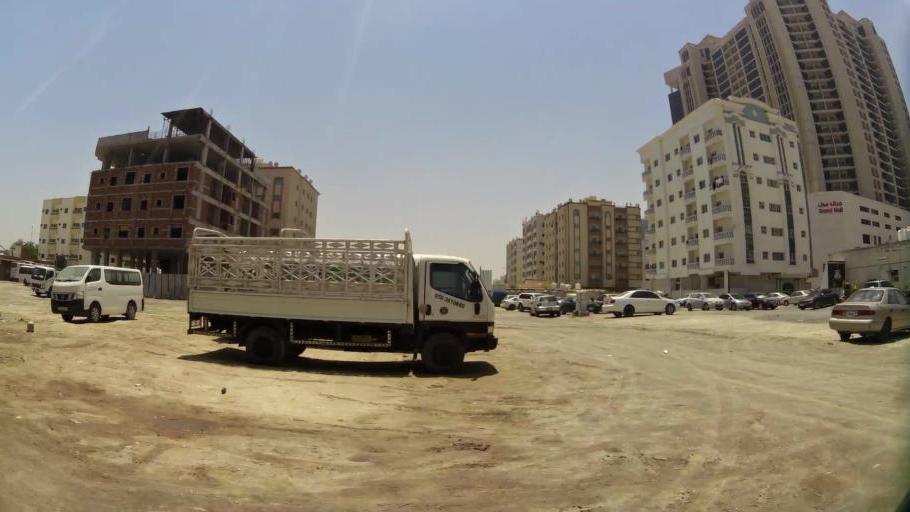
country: AE
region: Ajman
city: Ajman
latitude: 25.3942
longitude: 55.4388
